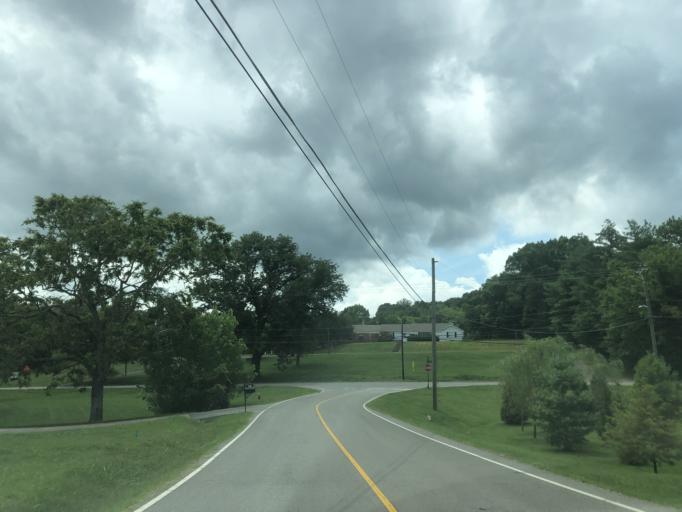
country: US
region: Tennessee
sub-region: Davidson County
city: Forest Hills
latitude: 36.0664
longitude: -86.8115
